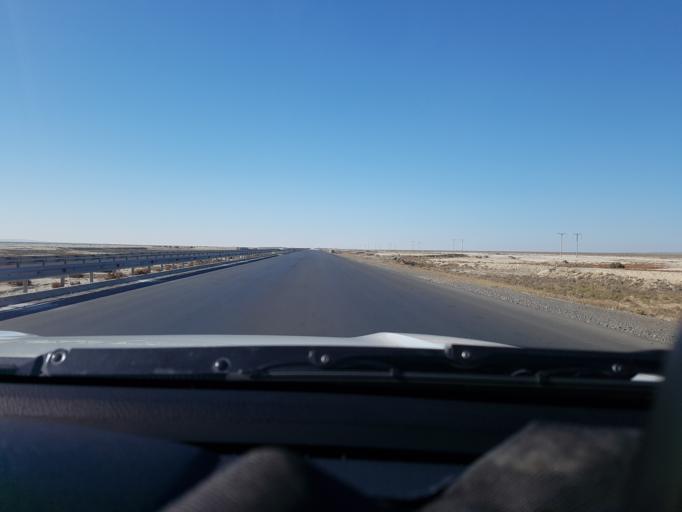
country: TM
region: Balkan
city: Gazanjyk
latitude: 39.2615
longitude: 55.1141
